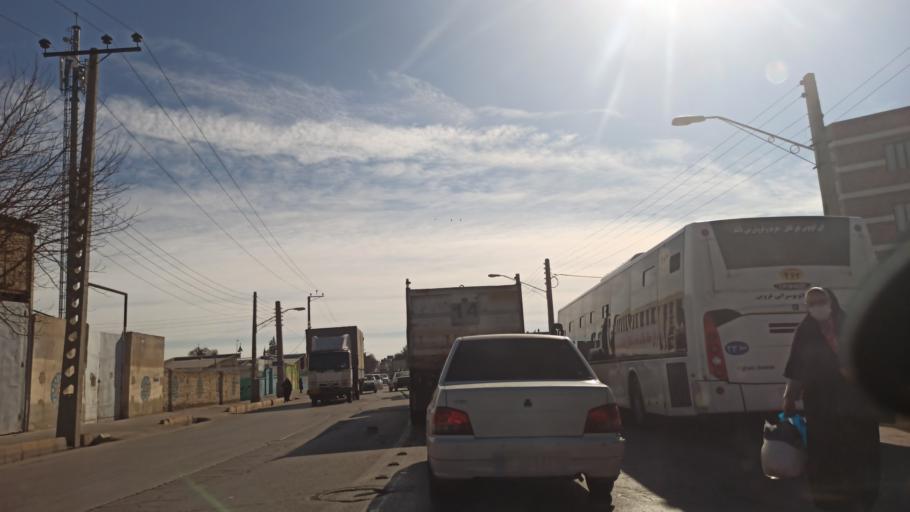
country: IR
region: Qazvin
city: Qazvin
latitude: 36.2532
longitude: 50.0007
